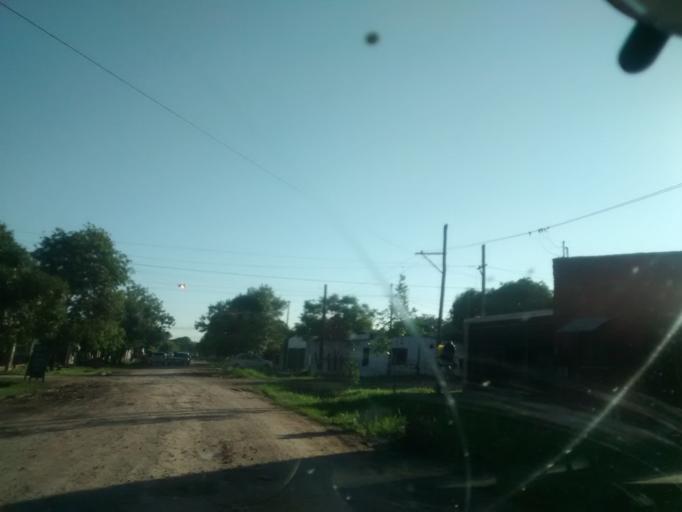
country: AR
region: Chaco
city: Resistencia
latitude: -27.4501
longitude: -59.0103
